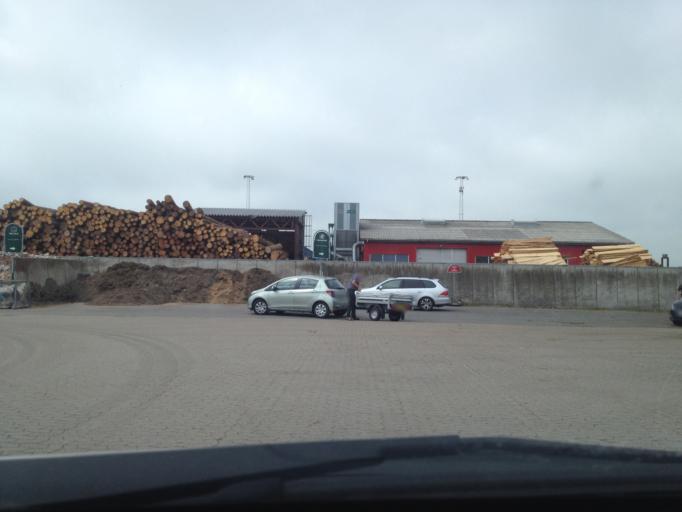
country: DK
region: South Denmark
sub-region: Esbjerg Kommune
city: Ribe
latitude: 55.3560
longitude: 8.7670
